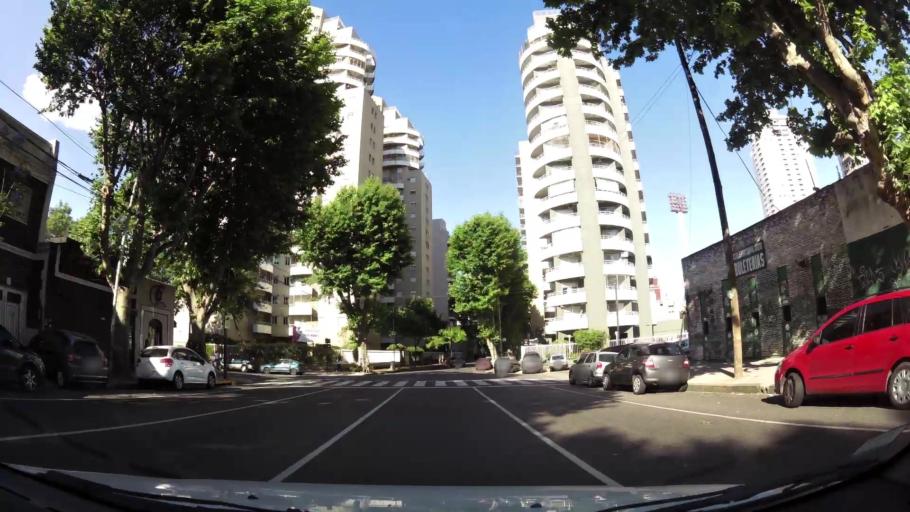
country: AR
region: Buenos Aires F.D.
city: Villa Santa Rita
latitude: -34.6180
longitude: -58.4483
